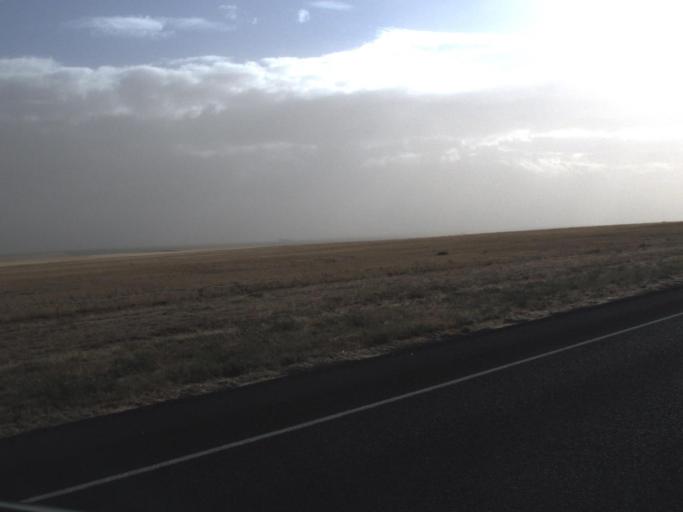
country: US
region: Washington
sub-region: Adams County
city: Ritzville
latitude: 47.4245
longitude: -118.3529
